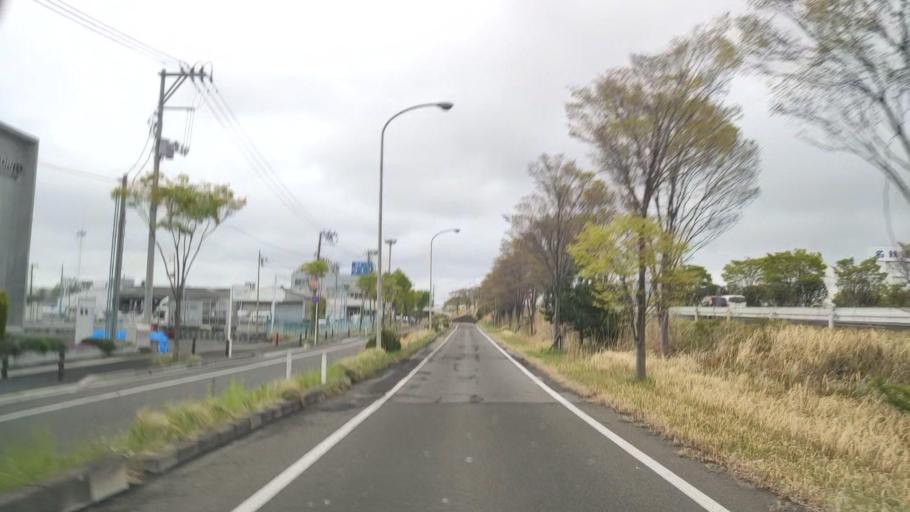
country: JP
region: Miyagi
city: Sendai-shi
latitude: 38.2656
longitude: 140.9380
